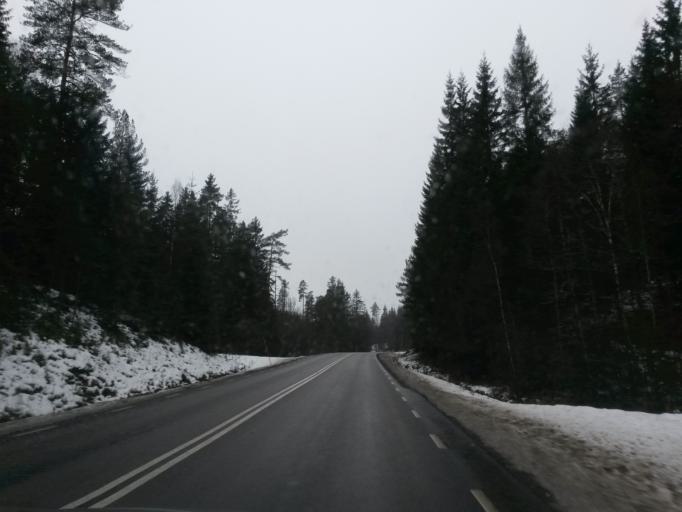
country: SE
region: Vaestra Goetaland
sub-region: Tranemo Kommun
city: Langhem
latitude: 57.6974
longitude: 13.2704
